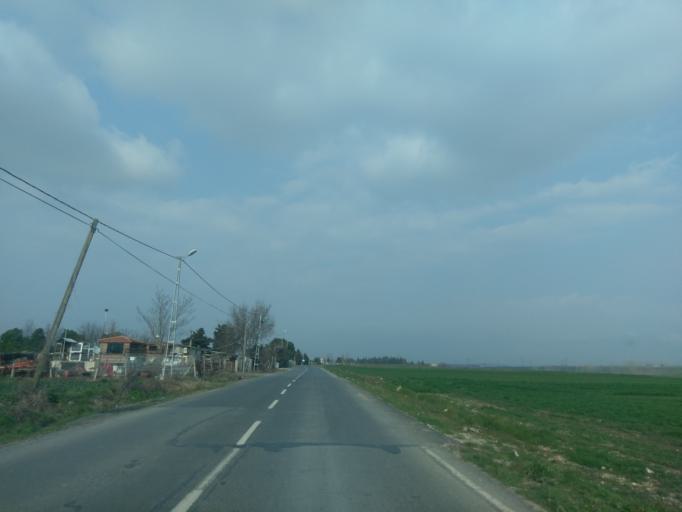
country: TR
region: Istanbul
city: Silivri
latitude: 41.0889
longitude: 28.2699
